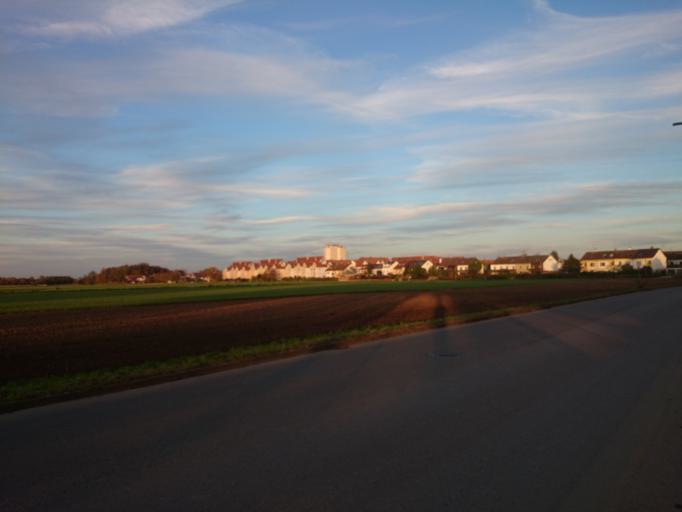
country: DE
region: Bavaria
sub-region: Swabia
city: Konigsbrunn
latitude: 48.2932
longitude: 10.8866
